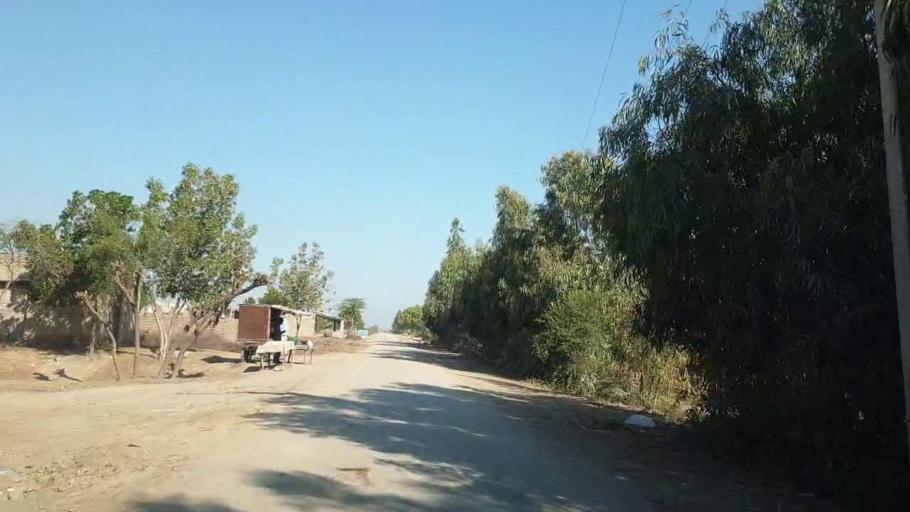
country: PK
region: Sindh
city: Mirpur Khas
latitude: 25.5794
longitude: 69.0459
